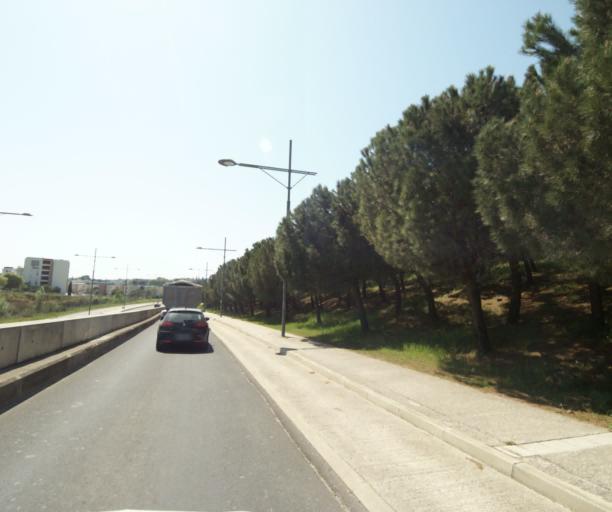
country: FR
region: Languedoc-Roussillon
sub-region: Departement de l'Herault
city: Montferrier-sur-Lez
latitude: 43.6401
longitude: 3.8466
